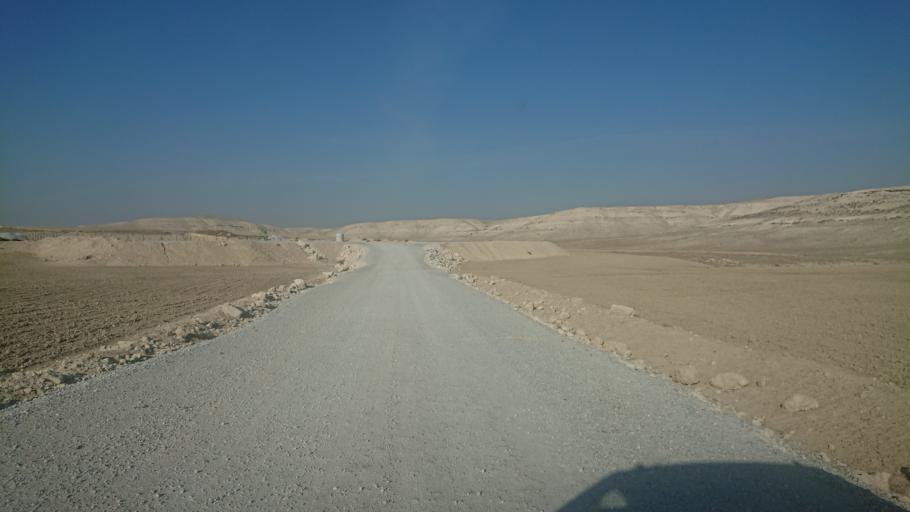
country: TR
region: Aksaray
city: Sultanhani
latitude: 38.0847
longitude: 33.6210
